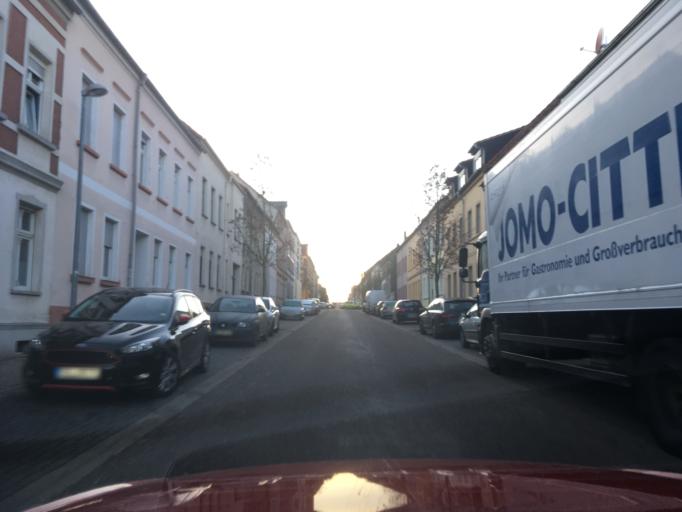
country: DE
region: Saxony-Anhalt
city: Rosslau
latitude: 51.8860
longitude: 12.2458
